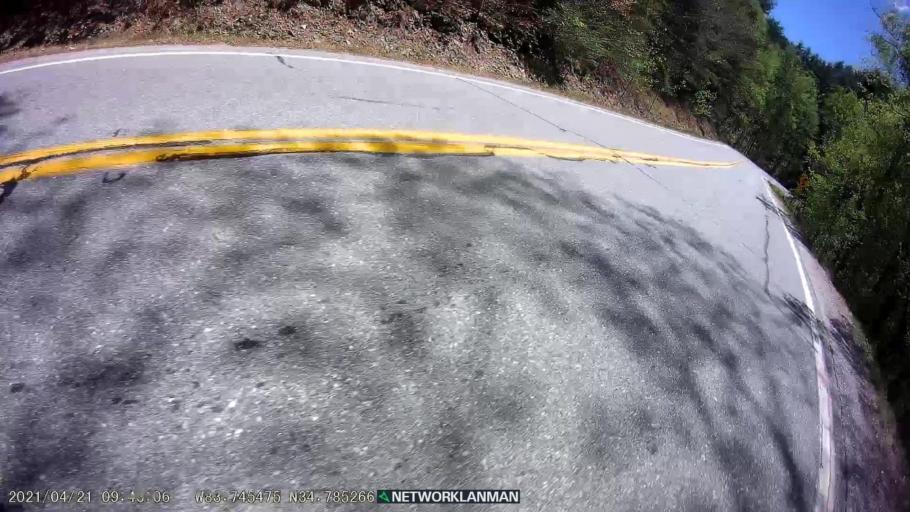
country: US
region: Georgia
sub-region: Towns County
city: Hiawassee
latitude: 34.7850
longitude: -83.7454
